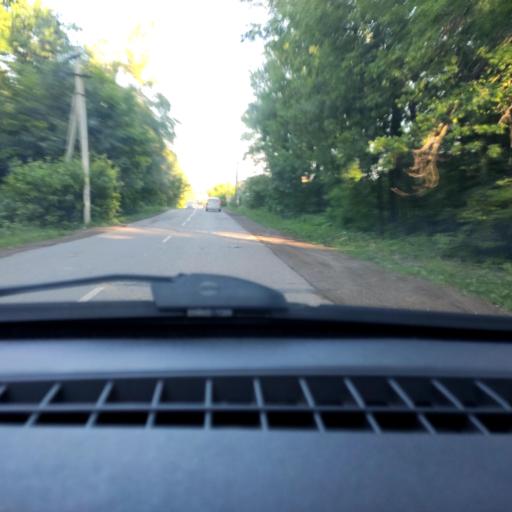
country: RU
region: Bashkortostan
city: Avdon
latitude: 54.6473
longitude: 55.7027
